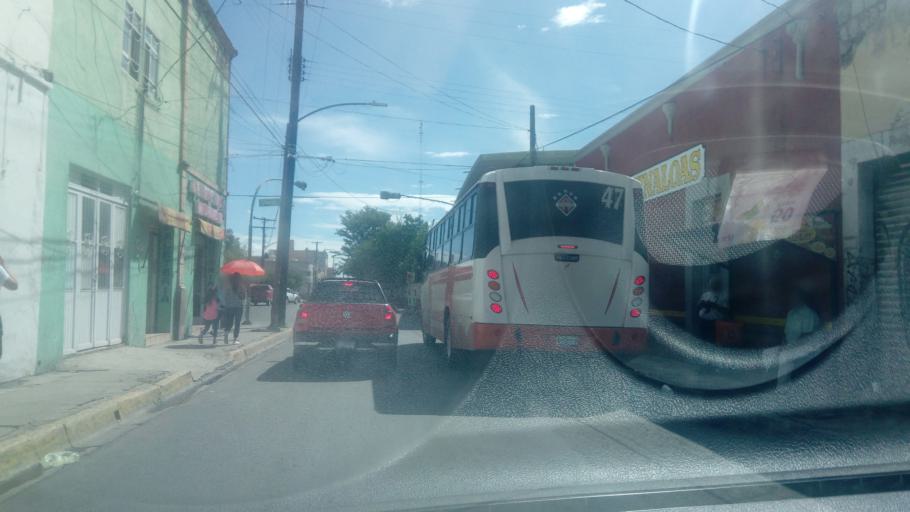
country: MX
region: Durango
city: Victoria de Durango
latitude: 24.0235
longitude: -104.6621
